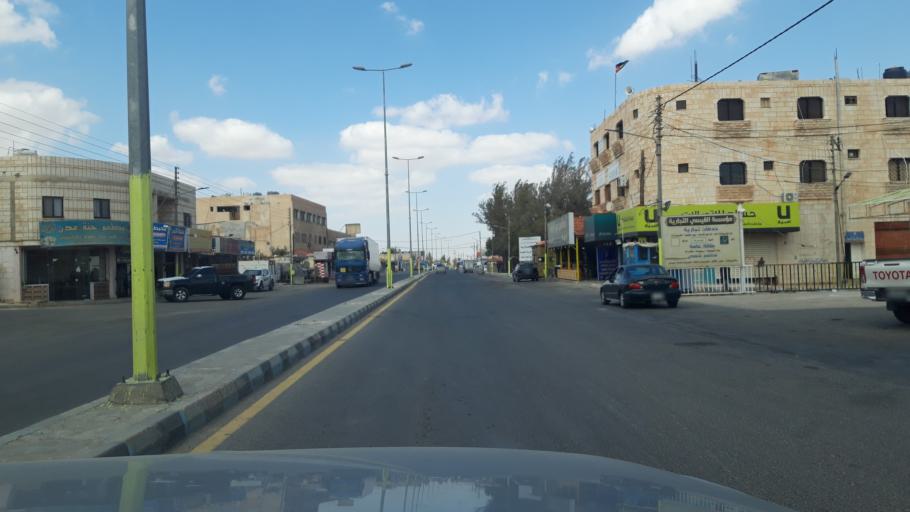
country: JO
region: Amman
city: Al Azraq ash Shamali
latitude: 31.8324
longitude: 36.8150
